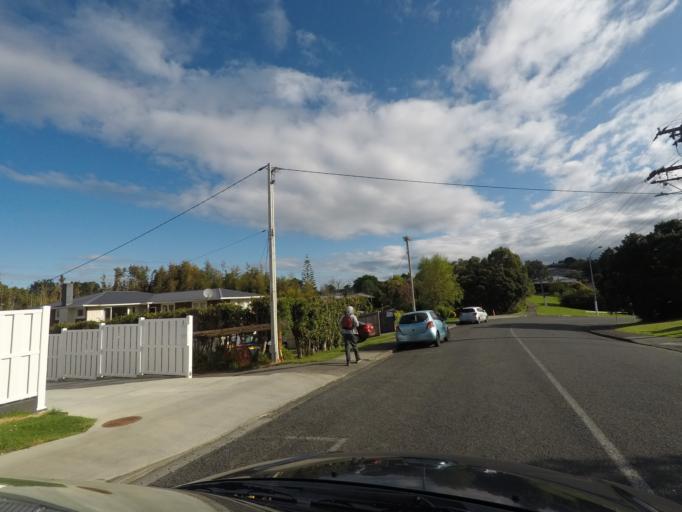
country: NZ
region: Auckland
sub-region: Auckland
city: Rosebank
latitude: -36.8813
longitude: 174.6529
